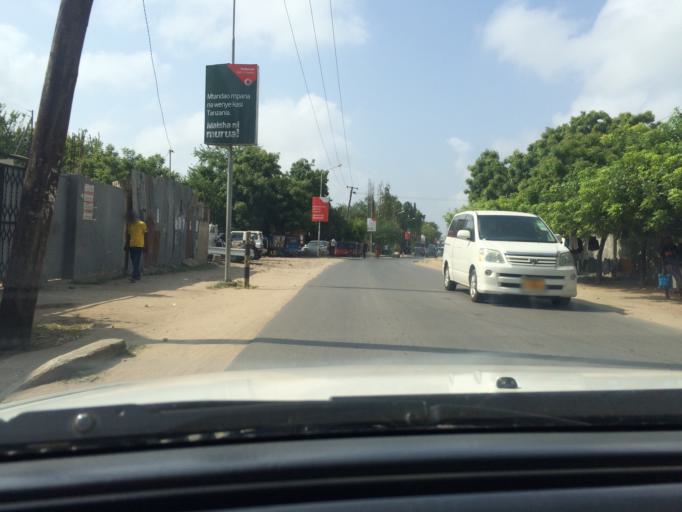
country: TZ
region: Dar es Salaam
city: Magomeni
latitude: -6.7610
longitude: 39.2709
